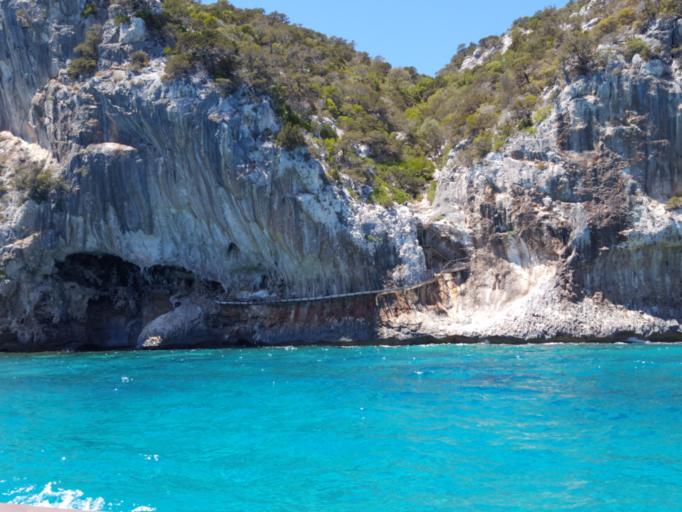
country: IT
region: Sardinia
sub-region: Provincia di Nuoro
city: Cala Gonone
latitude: 40.2494
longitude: 9.6243
